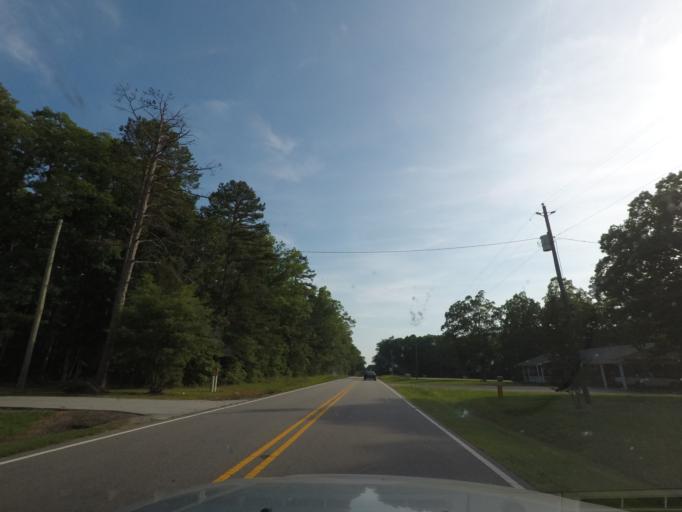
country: US
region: Virginia
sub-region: Mecklenburg County
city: Clarksville
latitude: 36.4887
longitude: -78.5464
